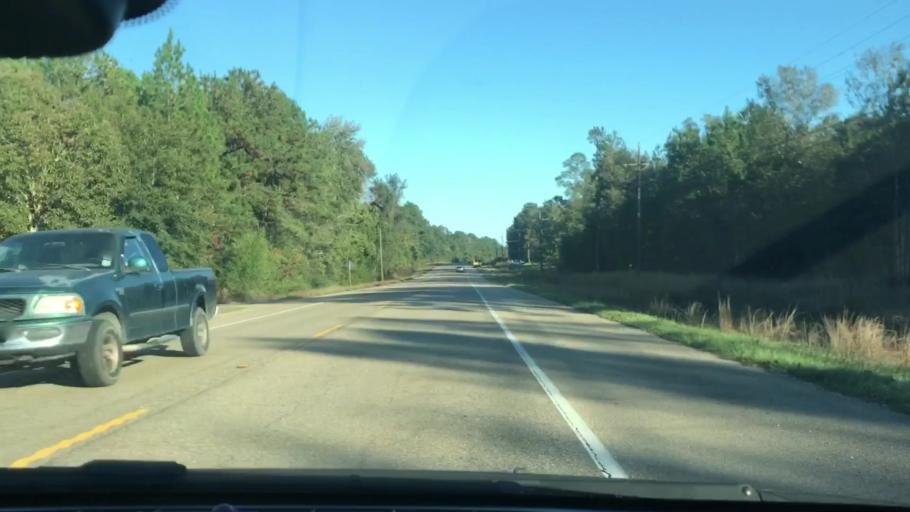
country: US
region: Louisiana
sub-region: Washington Parish
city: Bogalusa
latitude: 30.6089
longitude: -89.8858
